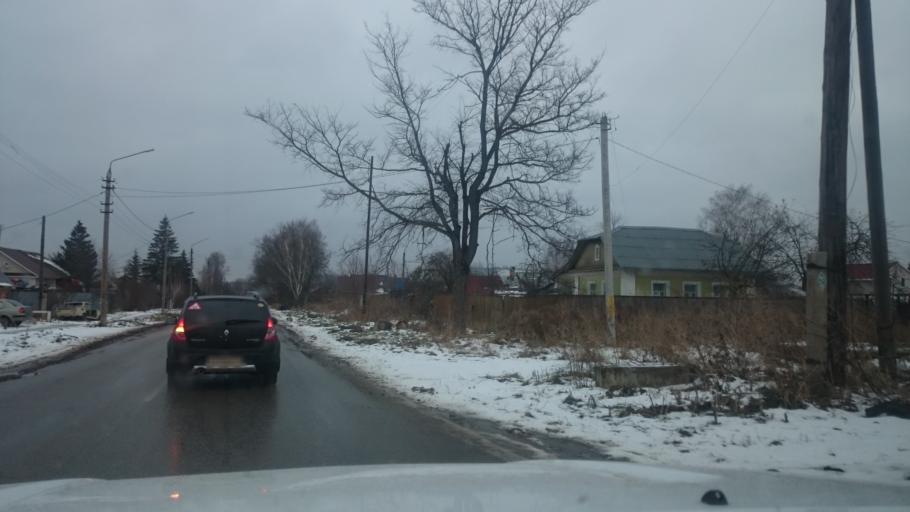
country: RU
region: Tula
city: Tula
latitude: 54.2028
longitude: 37.5557
